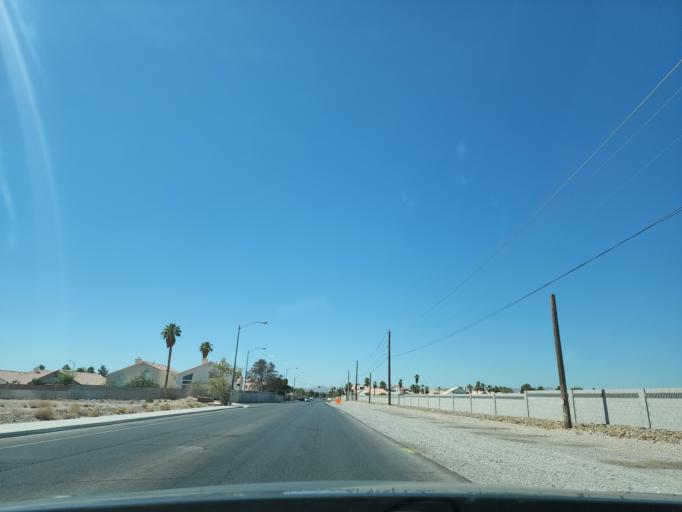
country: US
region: Nevada
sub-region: Clark County
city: Spring Valley
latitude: 36.1240
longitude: -115.2520
